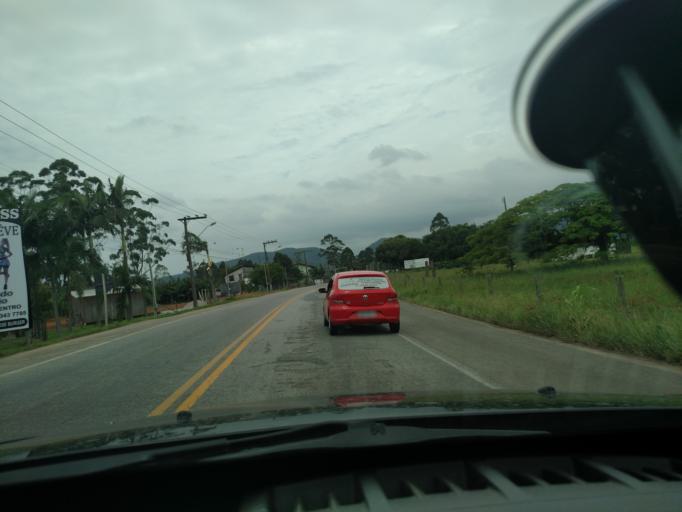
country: BR
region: Santa Catarina
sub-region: Itajai
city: Itajai
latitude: -26.8754
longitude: -48.7826
